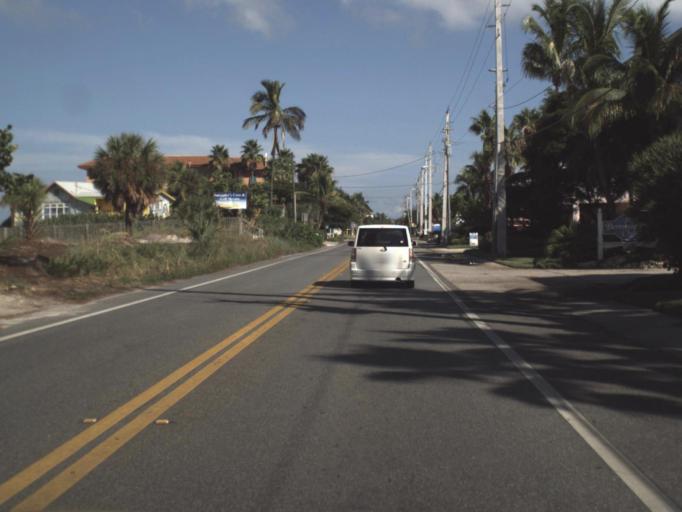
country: US
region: Florida
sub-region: Manatee County
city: Bradenton Beach
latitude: 27.4733
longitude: -82.7013
